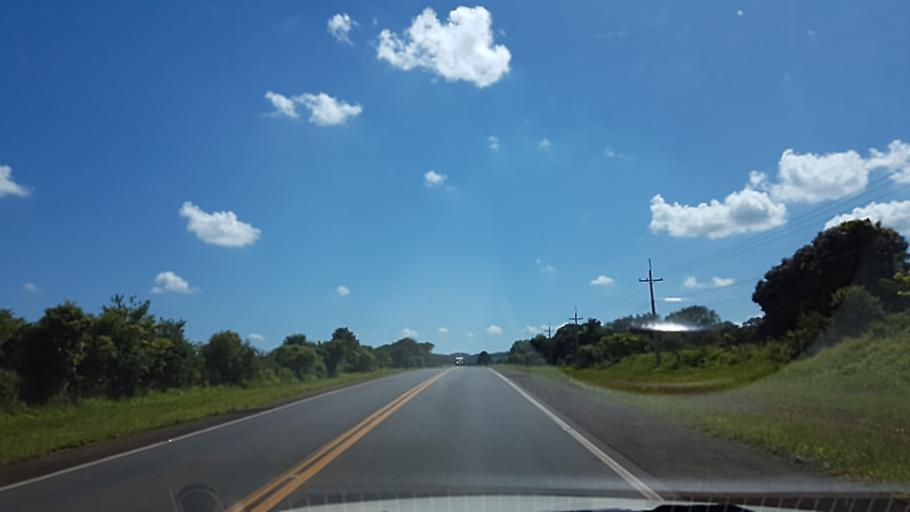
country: PY
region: Itapua
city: Carmen del Parana
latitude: -27.2168
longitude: -56.0941
